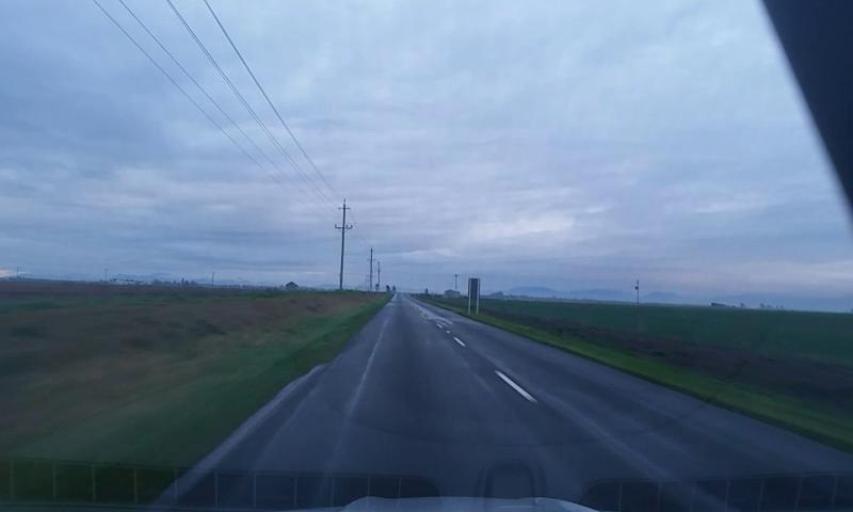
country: NZ
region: Canterbury
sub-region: Ashburton District
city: Rakaia
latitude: -43.7555
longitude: 171.9219
